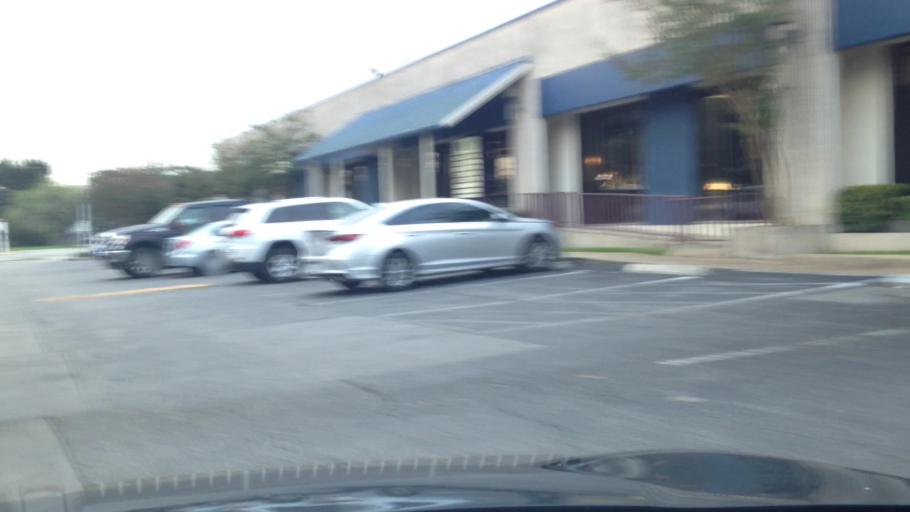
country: US
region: Texas
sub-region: Bexar County
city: Balcones Heights
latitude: 29.5106
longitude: -98.5687
